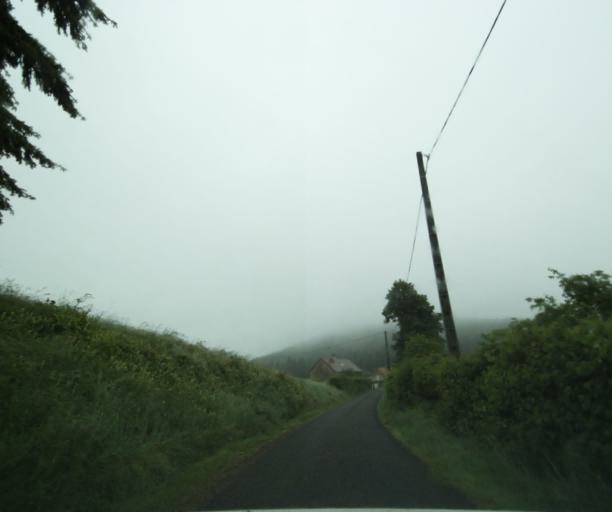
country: FR
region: Bourgogne
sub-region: Departement de Saone-et-Loire
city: Matour
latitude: 46.4033
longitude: 4.4056
